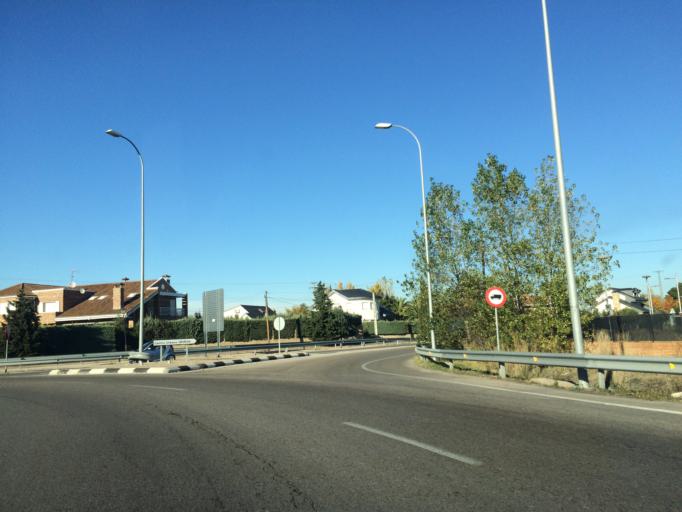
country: ES
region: Madrid
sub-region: Provincia de Madrid
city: Grinon
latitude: 40.2118
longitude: -3.8661
